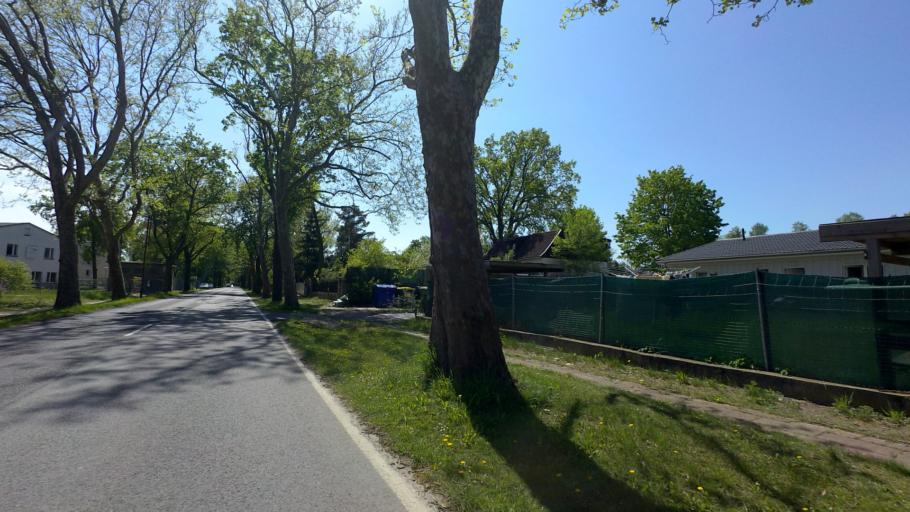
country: DE
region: Brandenburg
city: Bestensee
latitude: 52.2352
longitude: 13.6672
